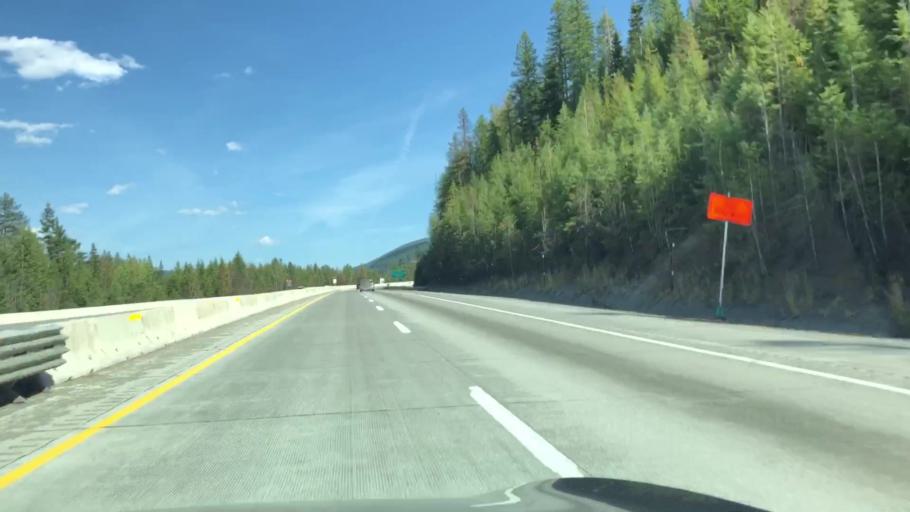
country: US
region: Idaho
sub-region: Shoshone County
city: Wallace
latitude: 47.4649
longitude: -115.7532
